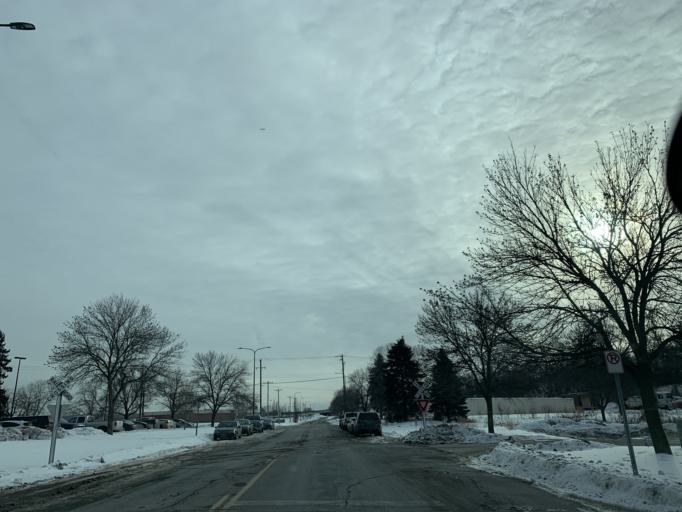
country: US
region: Minnesota
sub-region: Ramsey County
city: Saint Paul
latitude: 44.9351
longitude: -93.0774
